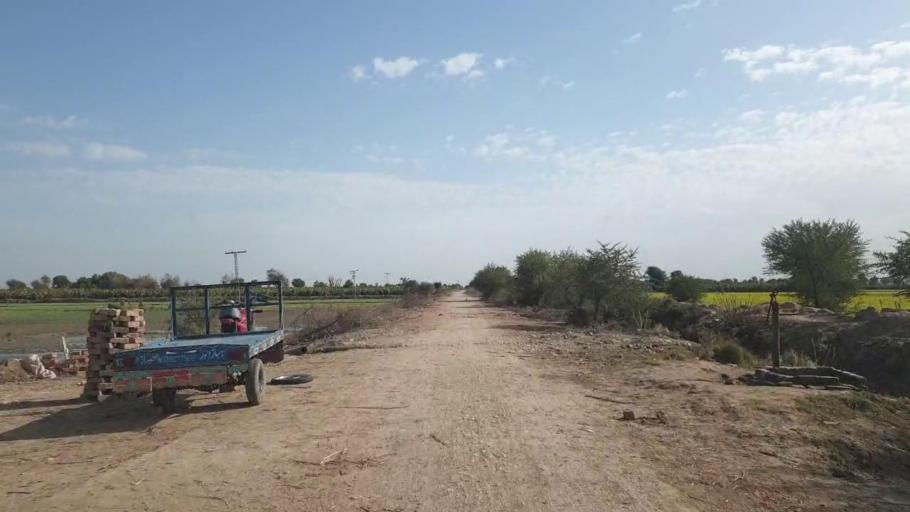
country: PK
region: Sindh
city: Shahdadpur
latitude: 26.0183
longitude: 68.4956
